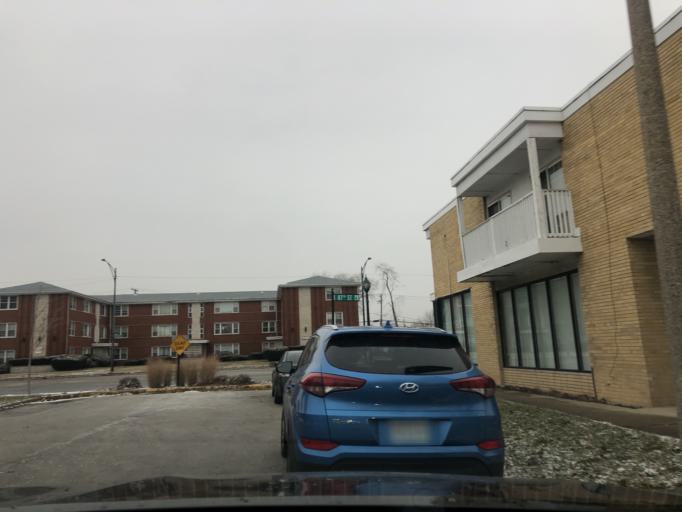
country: US
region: Illinois
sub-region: Cook County
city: Evergreen Park
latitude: 41.7350
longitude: -87.6935
